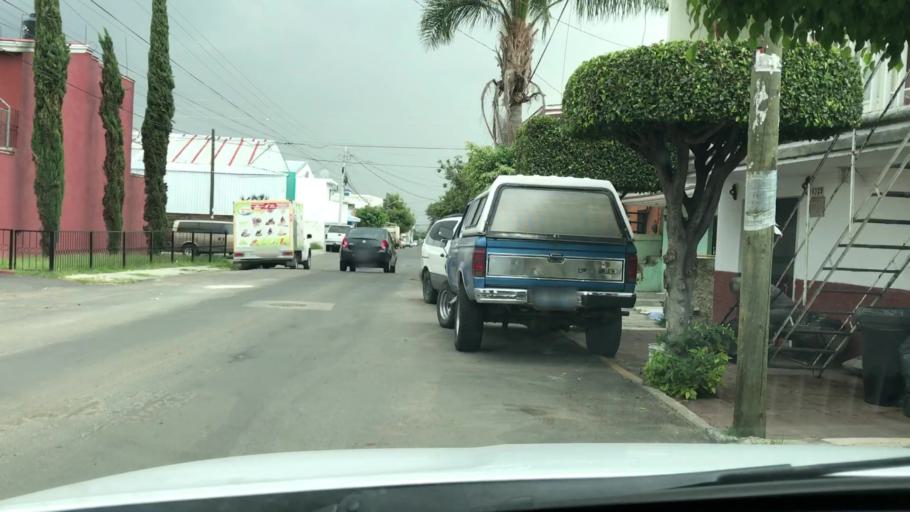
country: MX
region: Jalisco
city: Guadalajara
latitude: 20.6446
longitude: -103.4374
